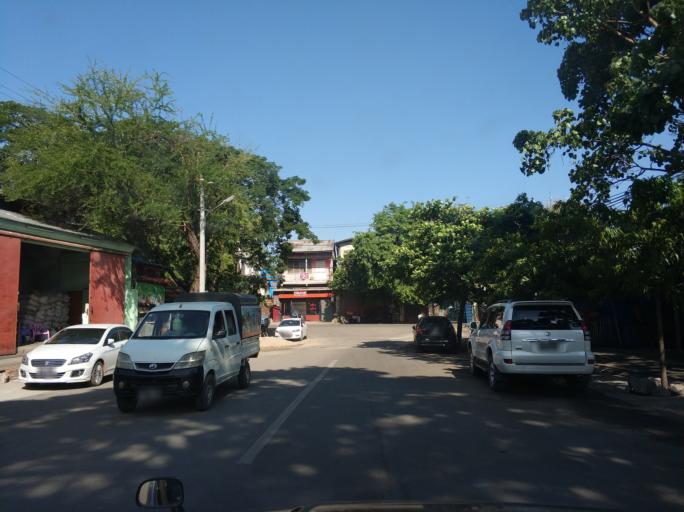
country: MM
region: Mandalay
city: Mandalay
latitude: 21.9731
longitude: 96.0726
